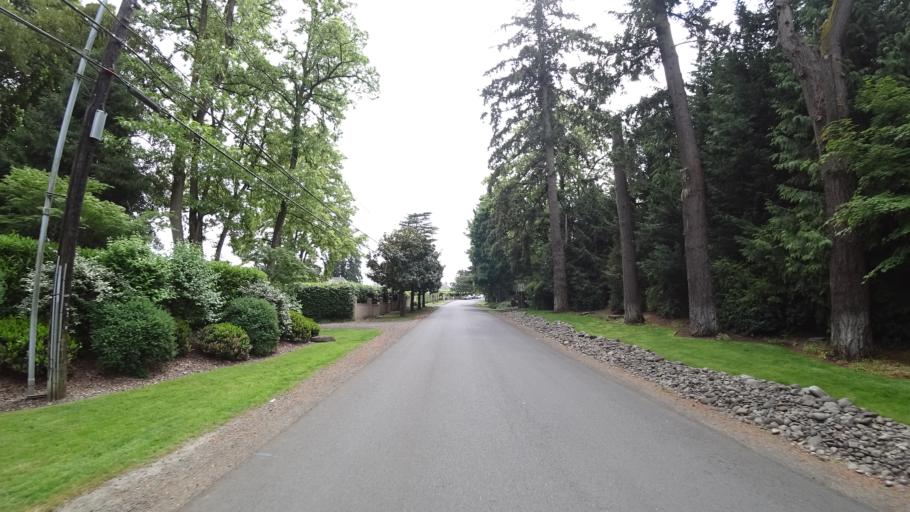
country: US
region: Oregon
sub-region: Washington County
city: Raleigh Hills
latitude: 45.4770
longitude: -122.7649
